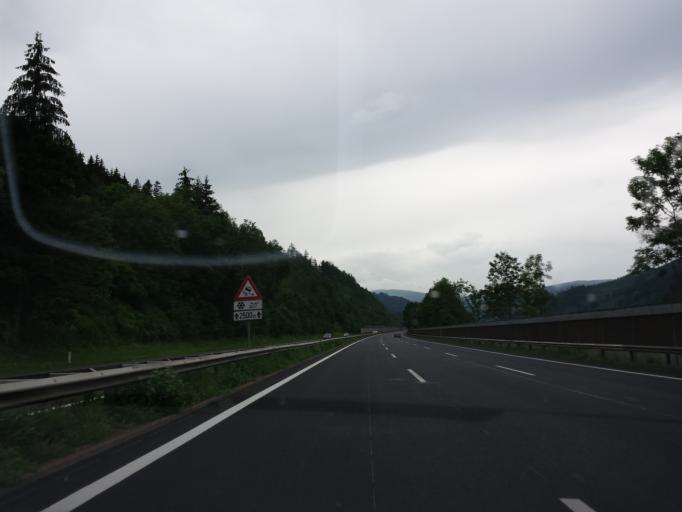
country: AT
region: Styria
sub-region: Politischer Bezirk Graz-Umgebung
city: Ubelbach
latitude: 47.2180
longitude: 15.2482
